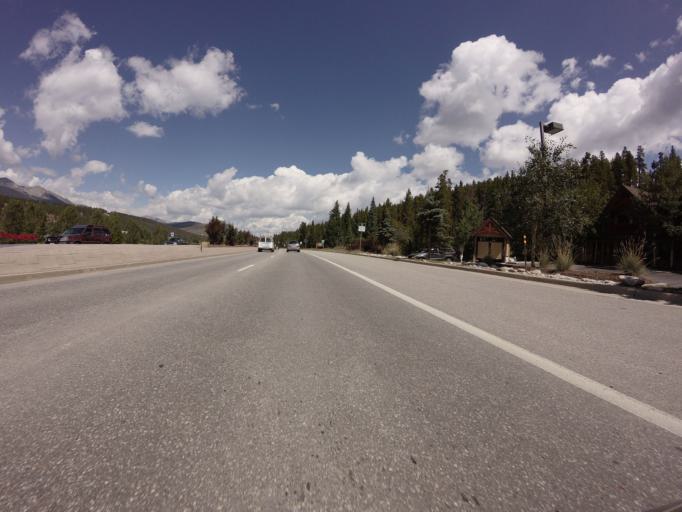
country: US
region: Colorado
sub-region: Summit County
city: Breckenridge
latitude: 39.4961
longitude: -106.0457
